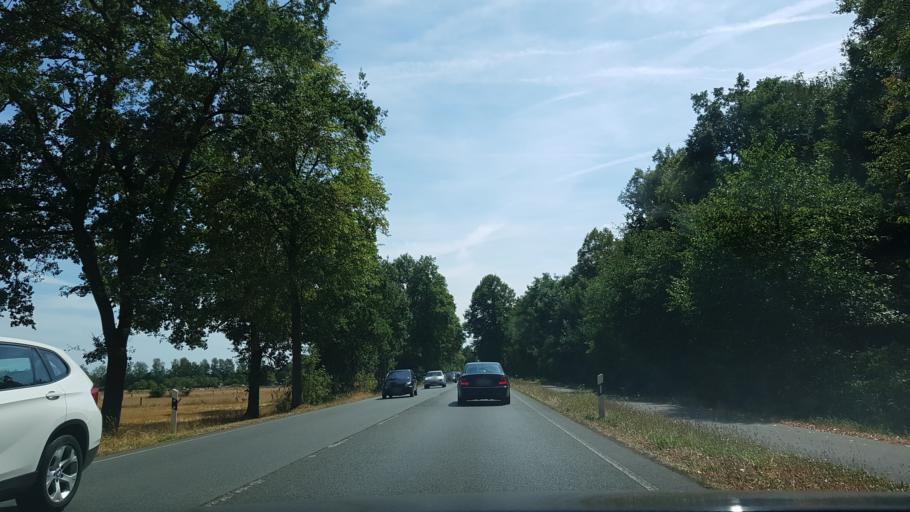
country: DE
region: North Rhine-Westphalia
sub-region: Regierungsbezirk Dusseldorf
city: Voerde
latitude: 51.6023
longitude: 6.7049
